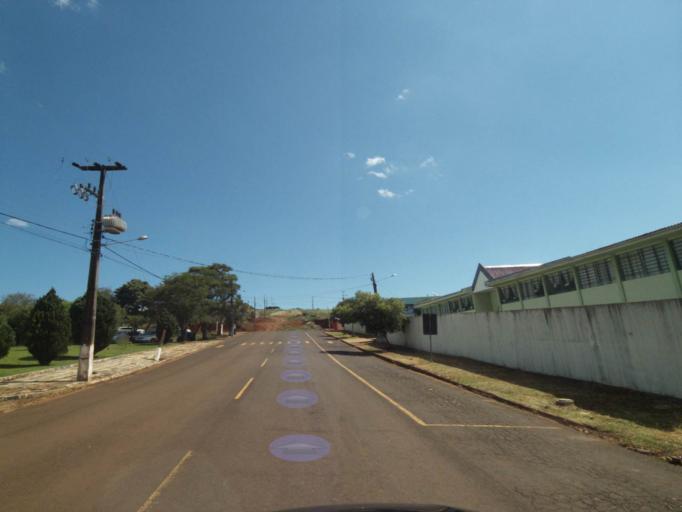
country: BR
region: Parana
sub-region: Coronel Vivida
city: Coronel Vivida
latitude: -26.1454
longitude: -52.3804
